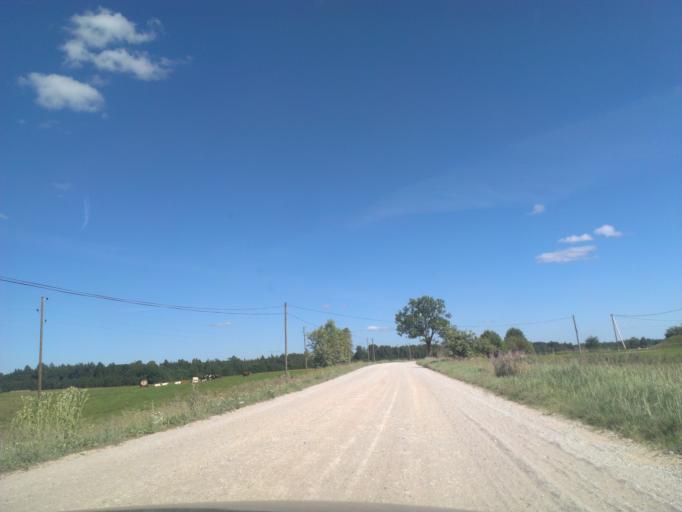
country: LV
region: Malpils
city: Malpils
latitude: 57.0158
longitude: 24.9948
